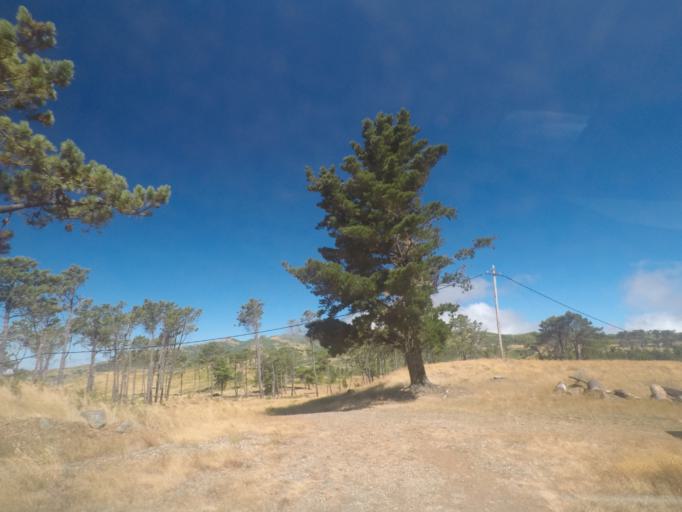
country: PT
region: Madeira
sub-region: Funchal
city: Nossa Senhora do Monte
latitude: 32.7097
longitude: -16.9106
